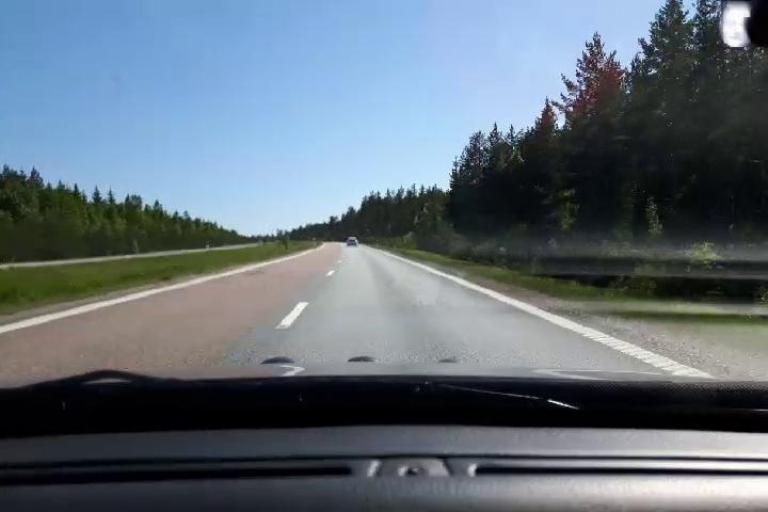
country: SE
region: Gaevleborg
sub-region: Soderhamns Kommun
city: Soderhamn
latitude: 61.4642
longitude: 16.9884
